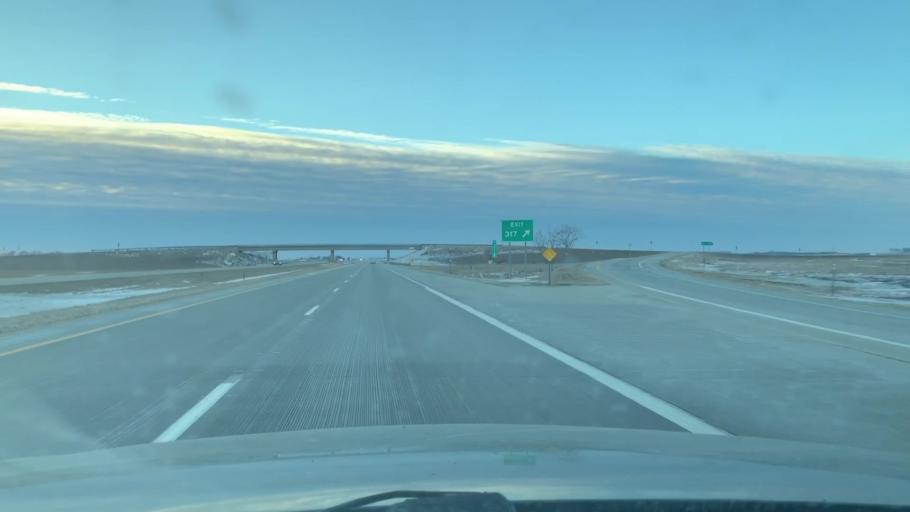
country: US
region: North Dakota
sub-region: Cass County
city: Casselton
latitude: 46.8758
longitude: -97.4893
